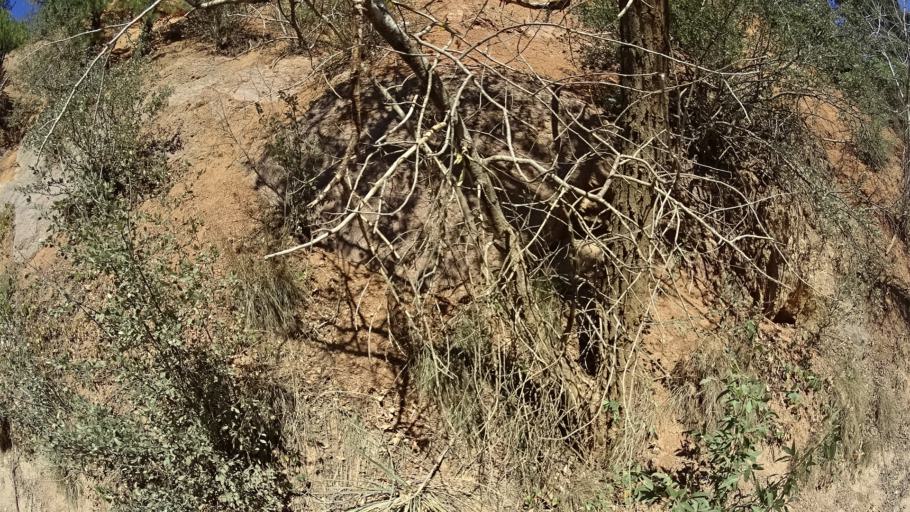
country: US
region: Colorado
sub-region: El Paso County
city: Manitou Springs
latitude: 38.7952
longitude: -104.8887
